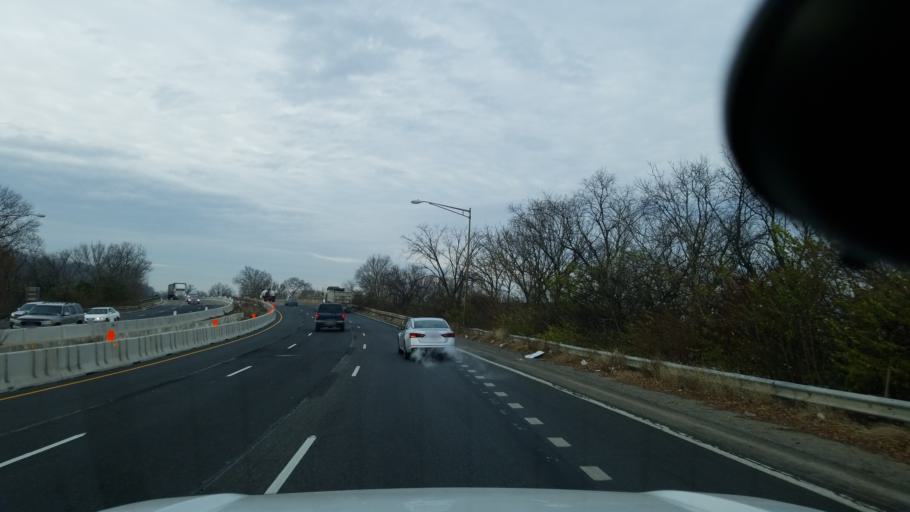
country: US
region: Maryland
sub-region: Prince George's County
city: Glassmanor
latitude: 38.8617
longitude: -77.0023
